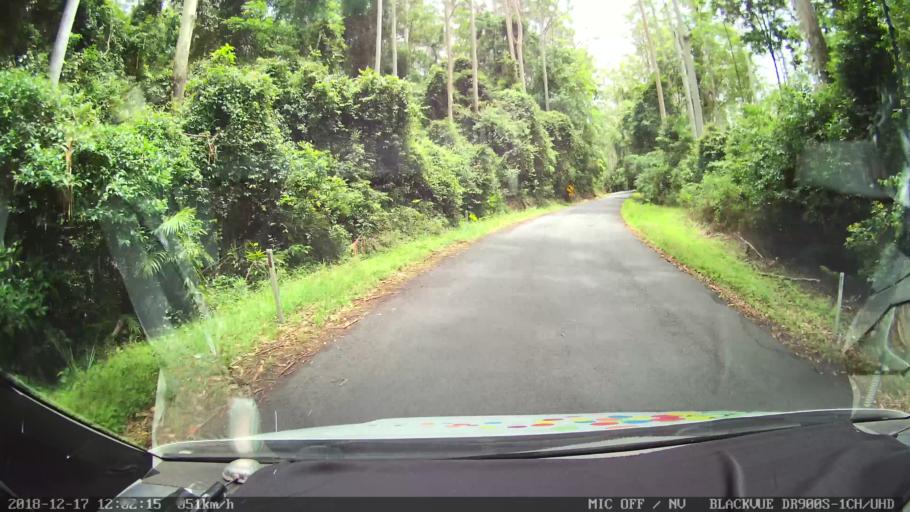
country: AU
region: New South Wales
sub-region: Kyogle
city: Kyogle
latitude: -28.5173
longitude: 152.5683
